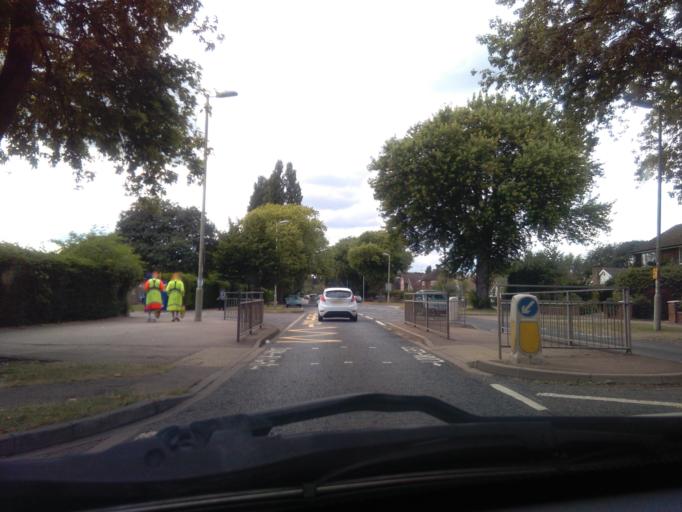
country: GB
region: England
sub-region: Bedford
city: Bedford
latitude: 52.1464
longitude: -0.4510
